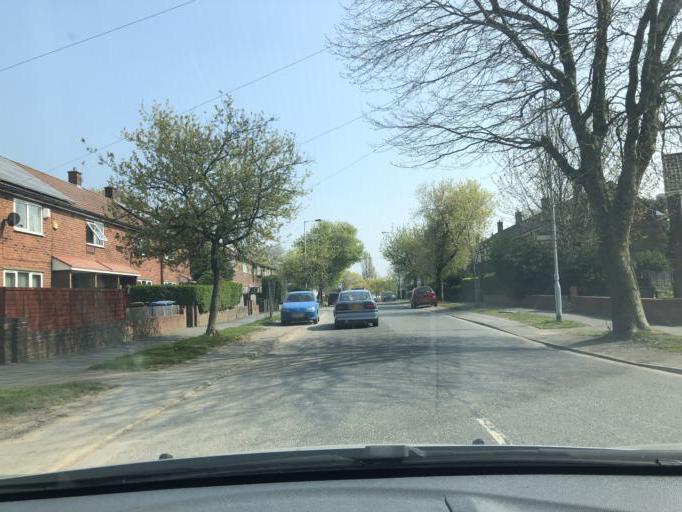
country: GB
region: England
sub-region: Borough of Stockport
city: Bredbury
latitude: 53.4310
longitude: -2.1329
